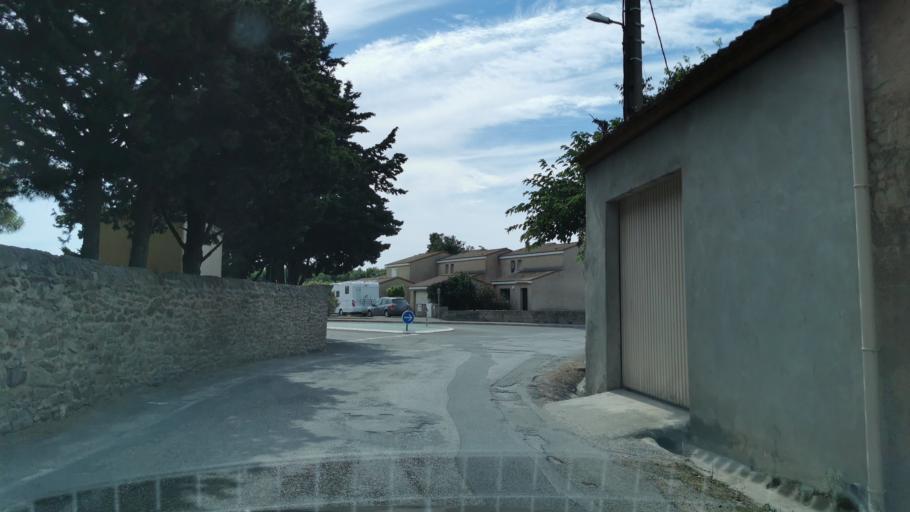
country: FR
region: Languedoc-Roussillon
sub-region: Departement de l'Herault
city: Olonzac
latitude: 43.2676
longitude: 2.7220
